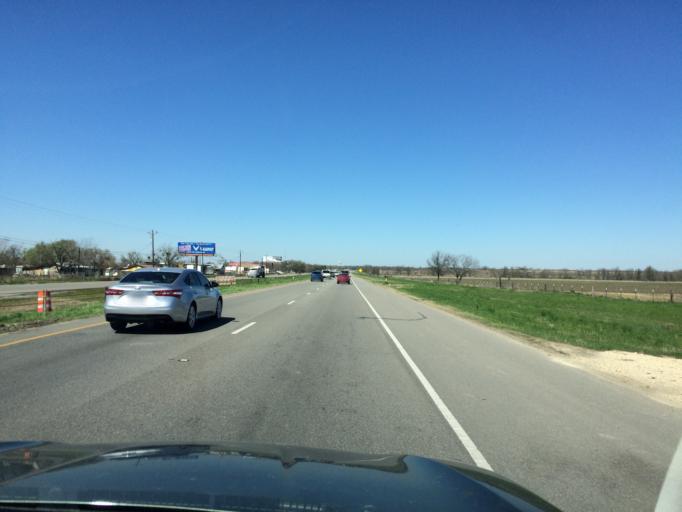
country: US
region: Texas
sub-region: Travis County
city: Garfield
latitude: 30.1764
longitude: -97.5290
